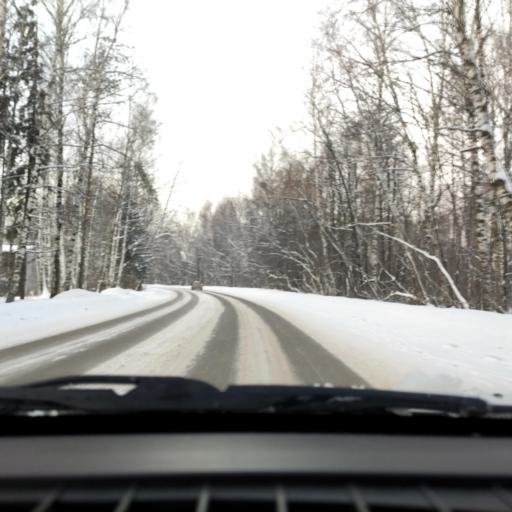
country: RU
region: Perm
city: Overyata
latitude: 58.0537
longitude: 55.8835
